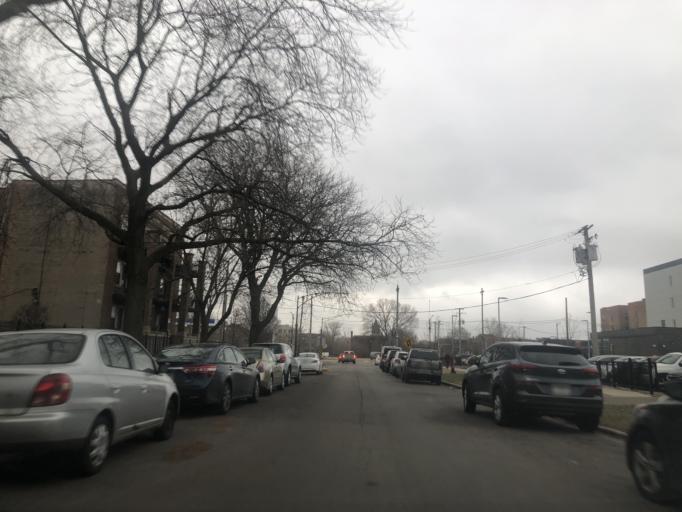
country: US
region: Illinois
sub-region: Cook County
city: Chicago
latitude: 41.7815
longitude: -87.6044
